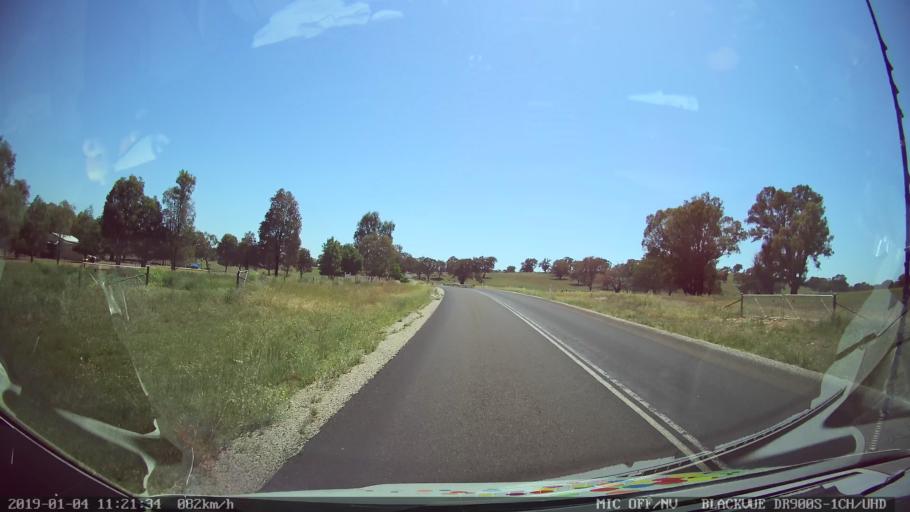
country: AU
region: New South Wales
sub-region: Cabonne
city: Molong
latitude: -33.1538
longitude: 148.7129
